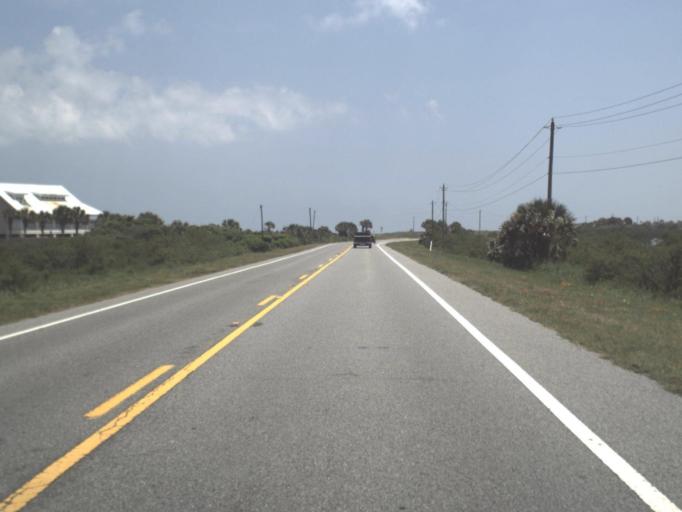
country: US
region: Florida
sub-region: Flagler County
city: Palm Coast
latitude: 29.6761
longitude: -81.2173
